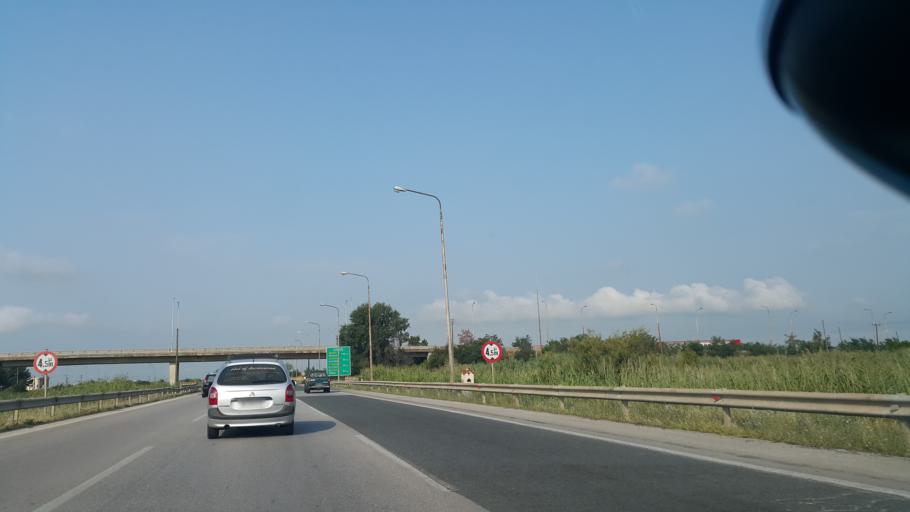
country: GR
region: Central Macedonia
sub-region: Nomos Thessalonikis
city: Sindos
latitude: 40.6456
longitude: 22.8041
